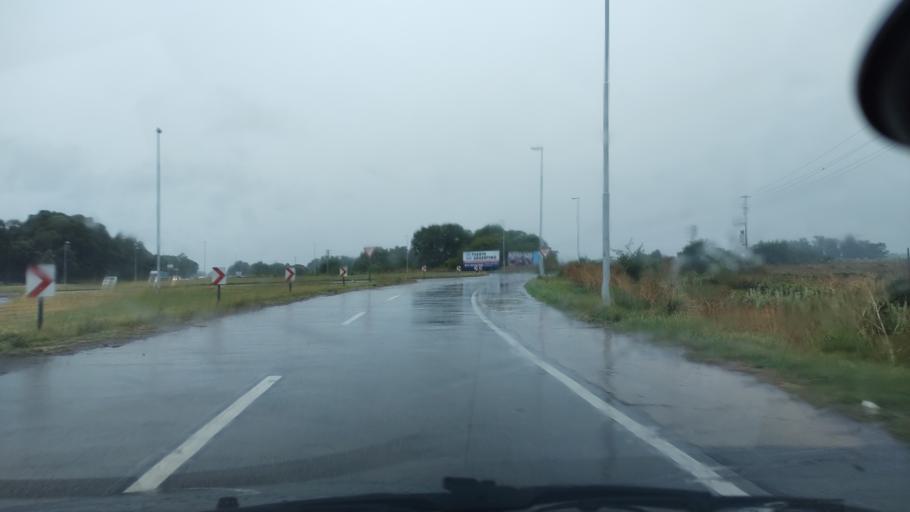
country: AR
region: Buenos Aires
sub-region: Partido de San Vicente
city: San Vicente
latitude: -35.0556
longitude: -58.4434
